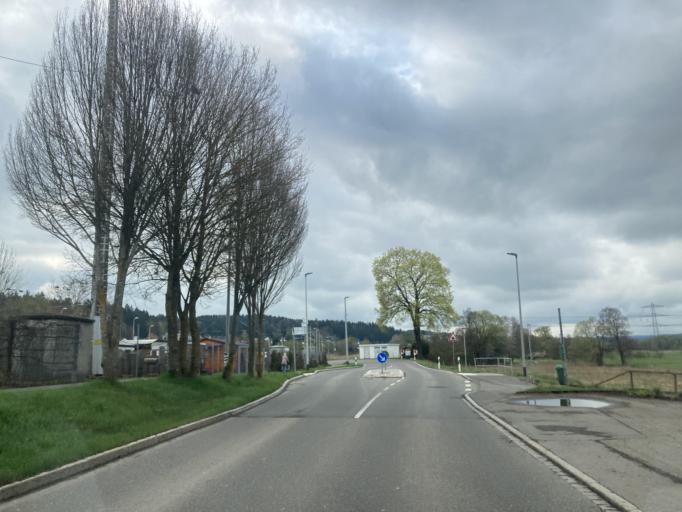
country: DE
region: Baden-Wuerttemberg
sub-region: Freiburg Region
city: Villingen-Schwenningen
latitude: 48.0322
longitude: 8.4683
